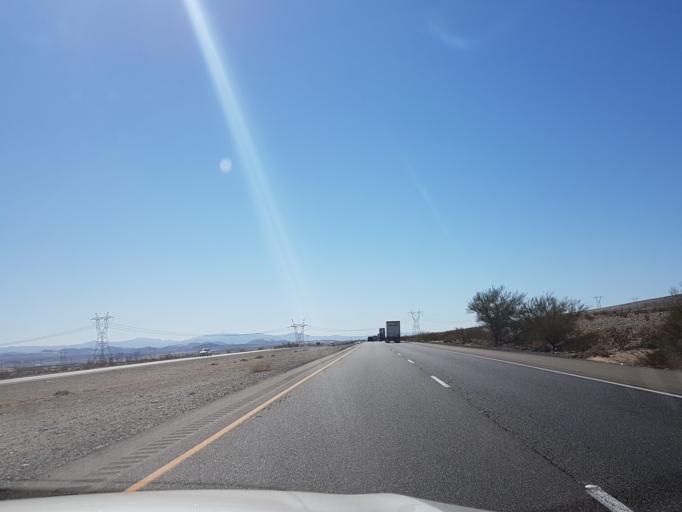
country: US
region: California
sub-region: San Bernardino County
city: Fort Irwin
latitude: 35.0563
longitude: -116.4351
